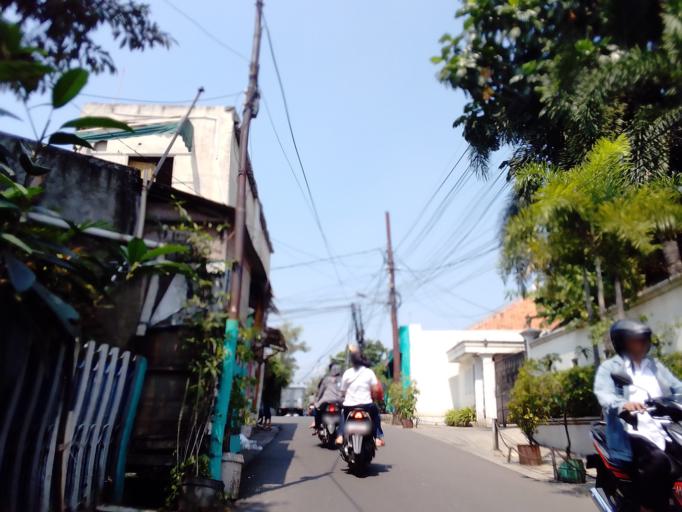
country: ID
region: Jakarta Raya
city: Jakarta
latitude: -6.2619
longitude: 106.8041
